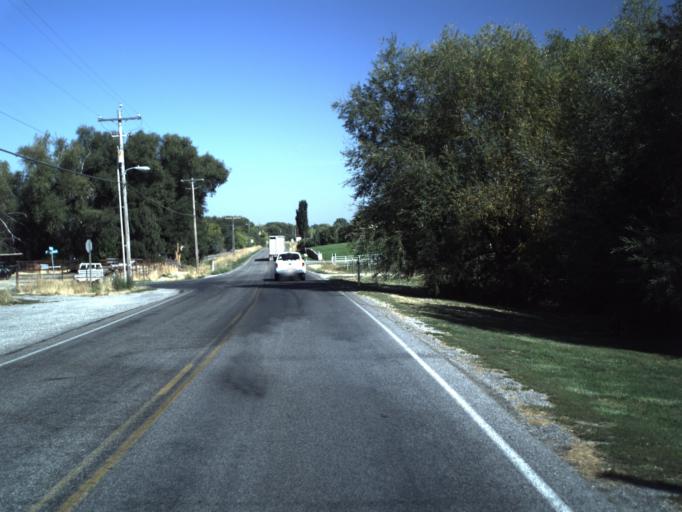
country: US
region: Utah
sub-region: Cache County
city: Hyrum
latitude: 41.5745
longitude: -111.8382
